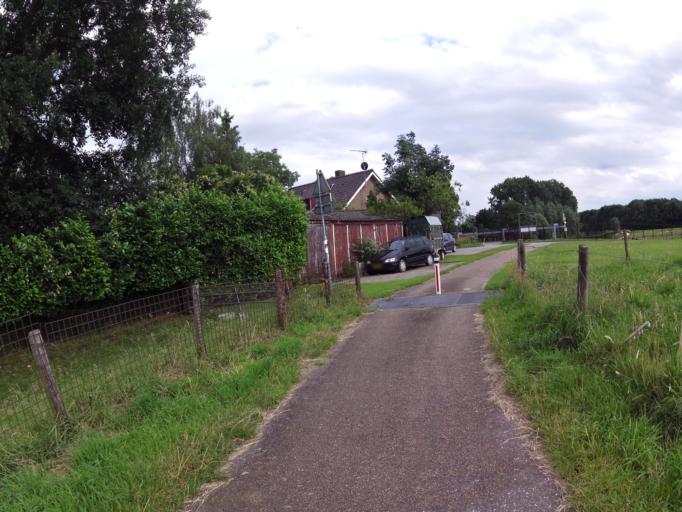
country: NL
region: North Brabant
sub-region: Gemeente Grave
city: Grave
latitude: 51.7691
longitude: 5.7295
